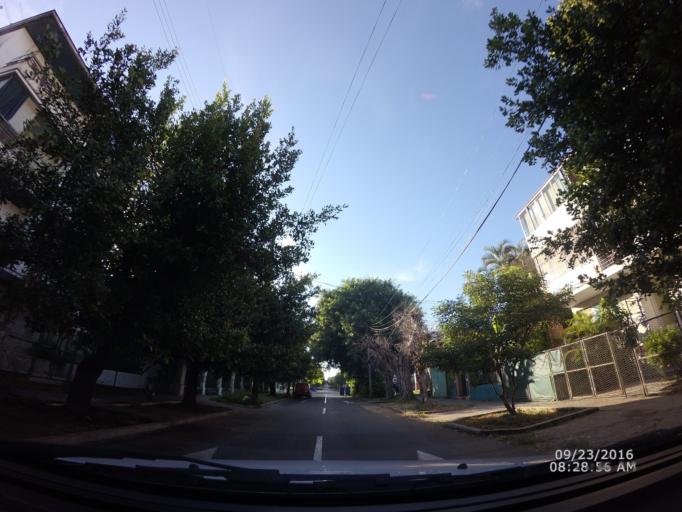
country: CU
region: La Habana
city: Havana
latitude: 23.1338
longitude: -82.3919
